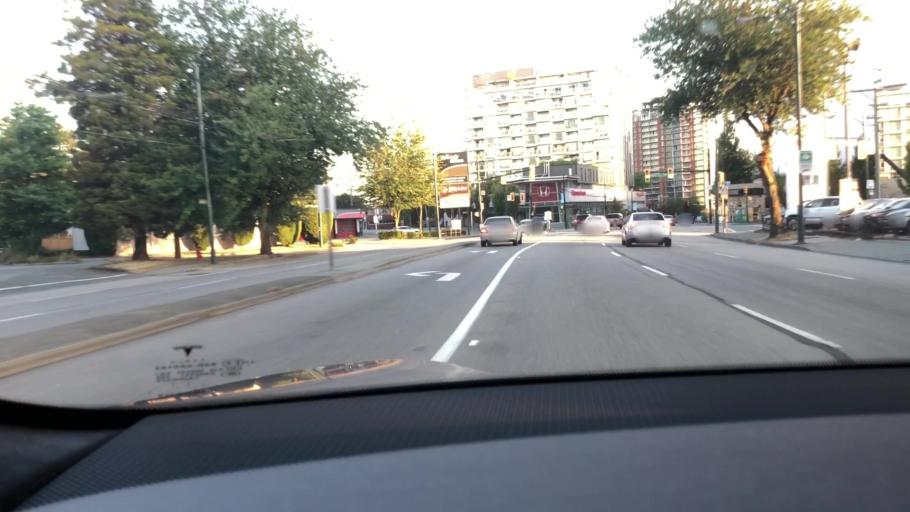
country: CA
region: British Columbia
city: Vancouver
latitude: 49.2592
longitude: -123.0956
